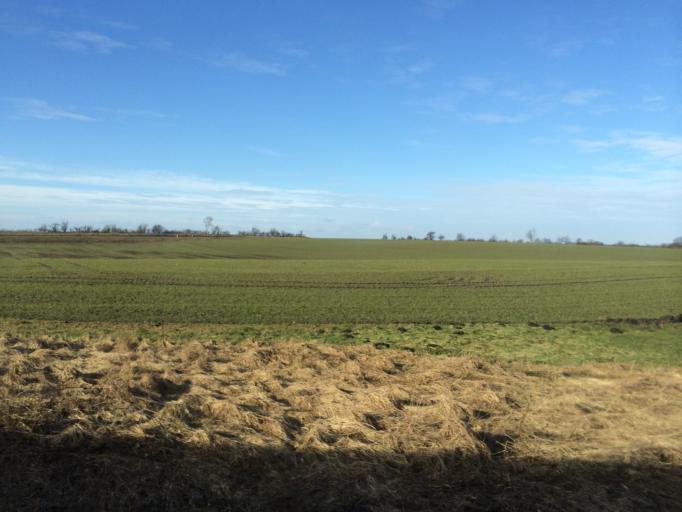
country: DK
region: South Denmark
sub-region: Vejle Kommune
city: Jelling
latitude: 55.7619
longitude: 9.4425
